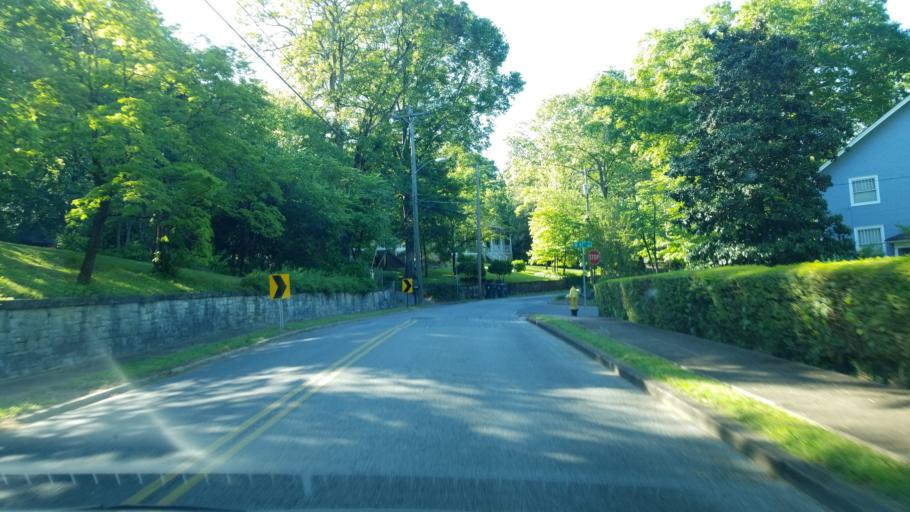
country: US
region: Tennessee
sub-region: Hamilton County
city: Lookout Mountain
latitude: 34.9959
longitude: -85.3267
